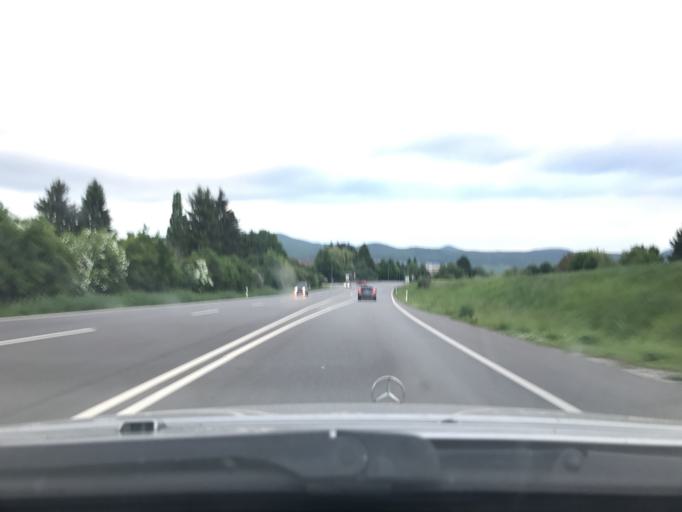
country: DE
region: Hesse
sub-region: Regierungsbezirk Kassel
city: Eschwege
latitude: 51.1803
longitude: 10.0375
